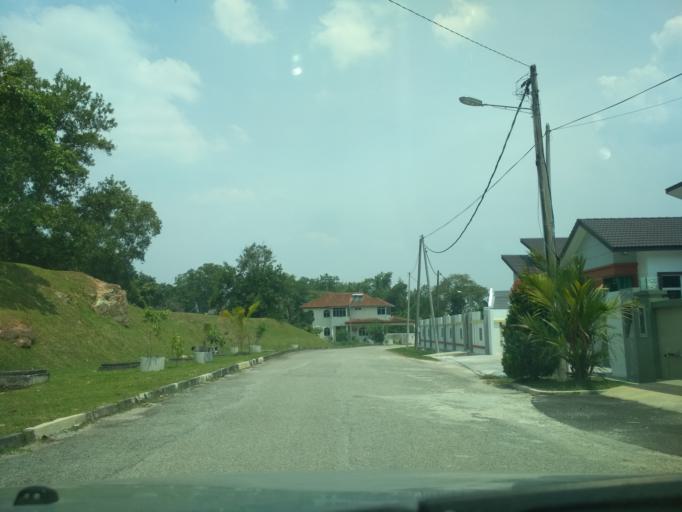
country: MY
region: Kedah
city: Kulim
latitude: 5.3649
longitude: 100.5340
